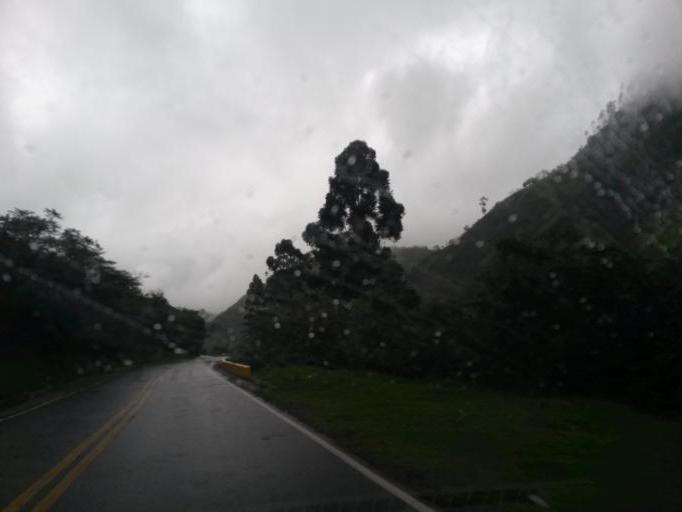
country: CO
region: Cauca
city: Popayan
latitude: 2.3723
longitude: -76.4925
